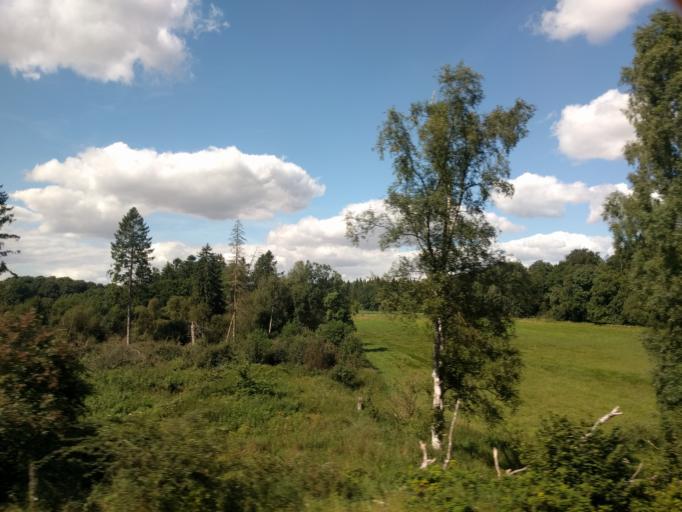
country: DK
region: Zealand
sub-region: Koge Kommune
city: Borup
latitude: 55.4591
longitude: 11.9207
